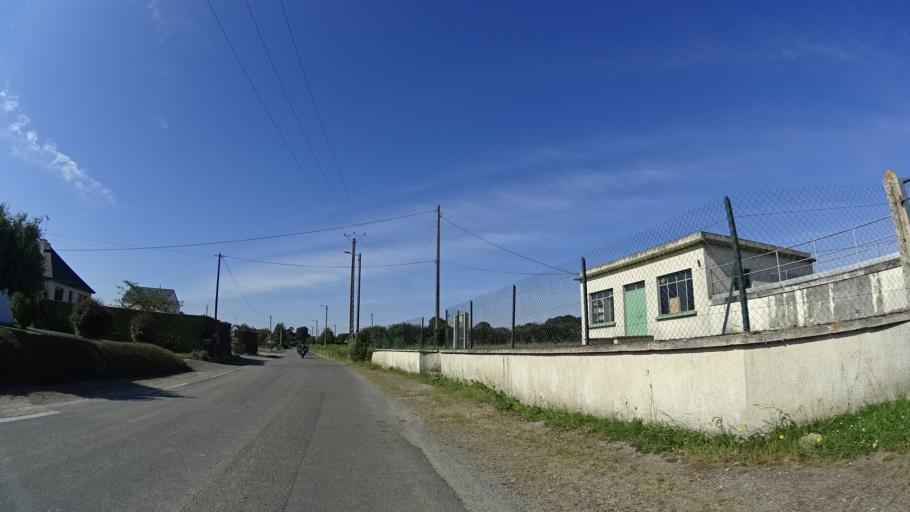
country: FR
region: Brittany
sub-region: Departement d'Ille-et-Vilaine
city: Guipry
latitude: 47.8177
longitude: -1.8480
